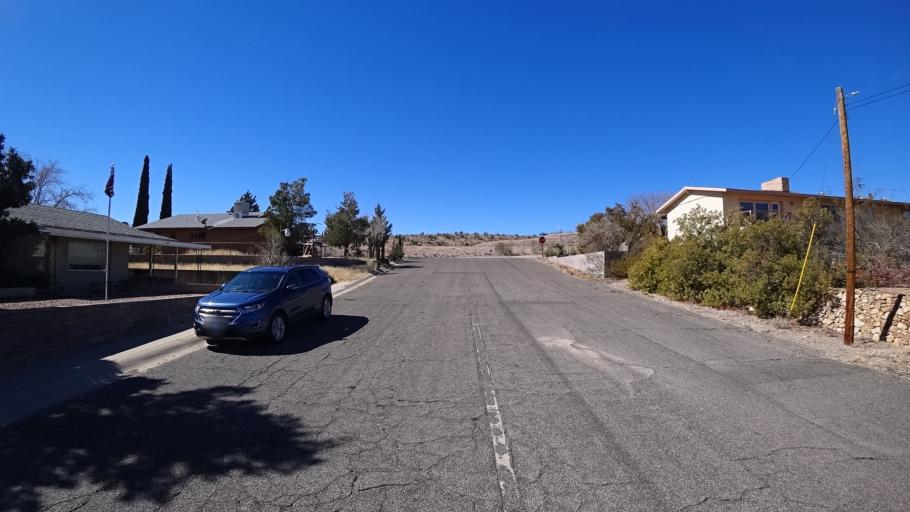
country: US
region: Arizona
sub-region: Mohave County
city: Kingman
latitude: 35.1946
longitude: -114.0659
